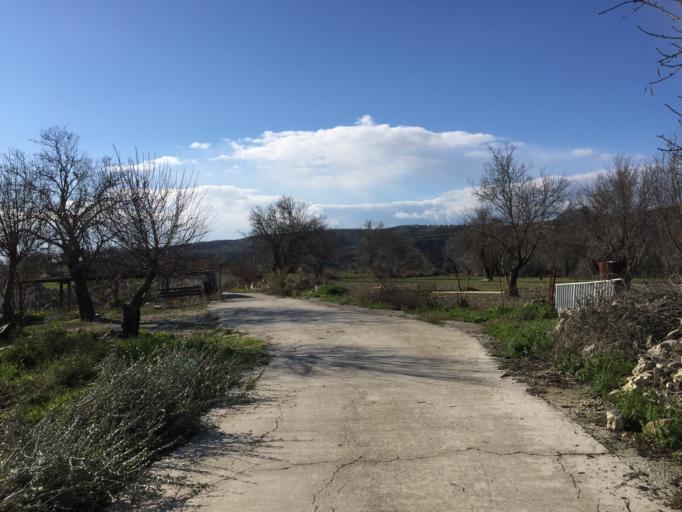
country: CY
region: Pafos
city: Mesogi
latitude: 34.8391
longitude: 32.5101
